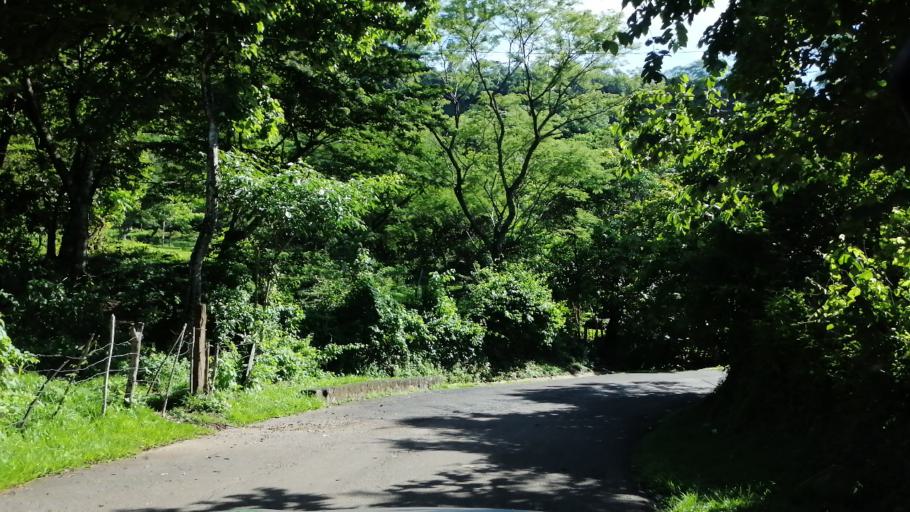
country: SV
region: Morazan
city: Corinto
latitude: 13.7950
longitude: -88.0113
